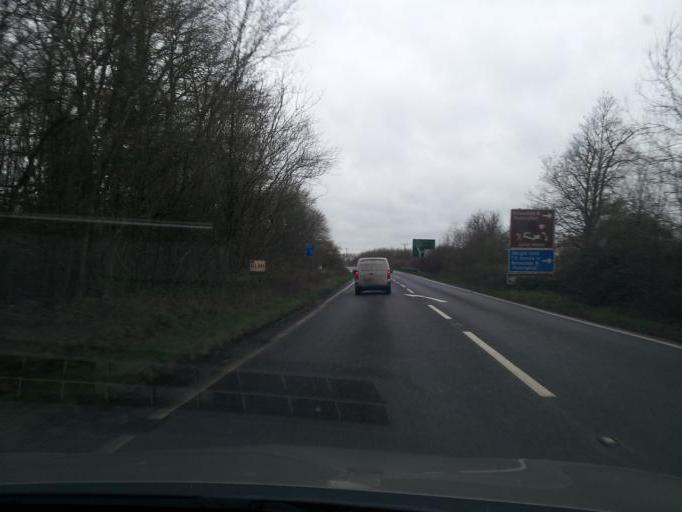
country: GB
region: England
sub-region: Suffolk
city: Botesdale
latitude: 52.3446
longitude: 1.0331
